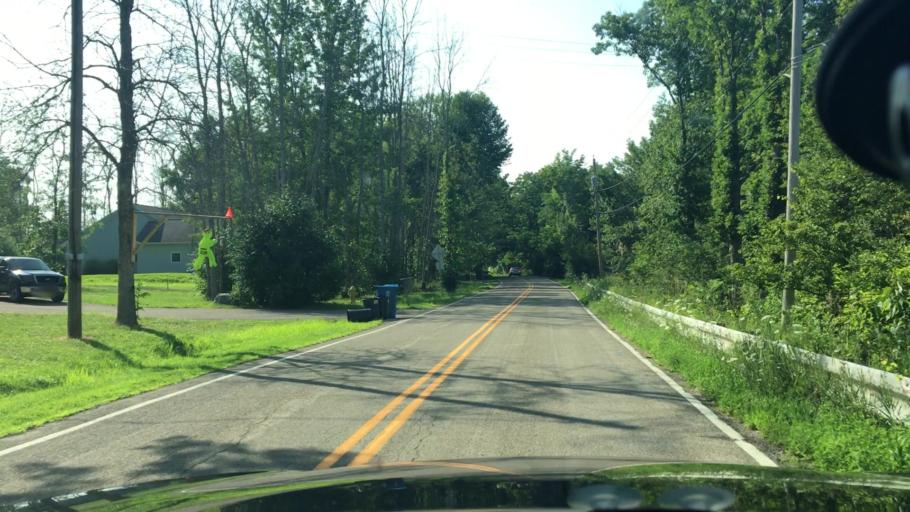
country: US
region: New York
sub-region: Erie County
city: North Collins
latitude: 42.6244
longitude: -78.9703
